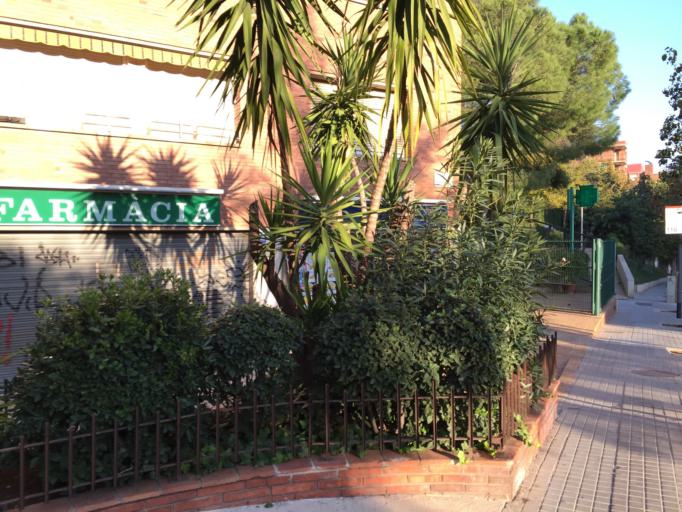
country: ES
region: Catalonia
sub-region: Provincia de Barcelona
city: Horta-Guinardo
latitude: 41.4146
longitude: 2.1582
